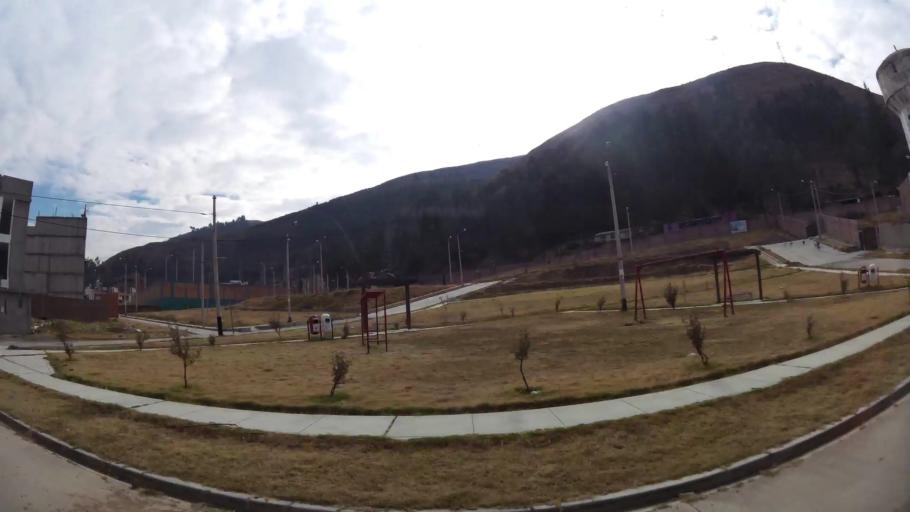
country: PE
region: Junin
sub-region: Provincia de Huancayo
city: Huancayo
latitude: -12.0490
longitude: -75.1871
